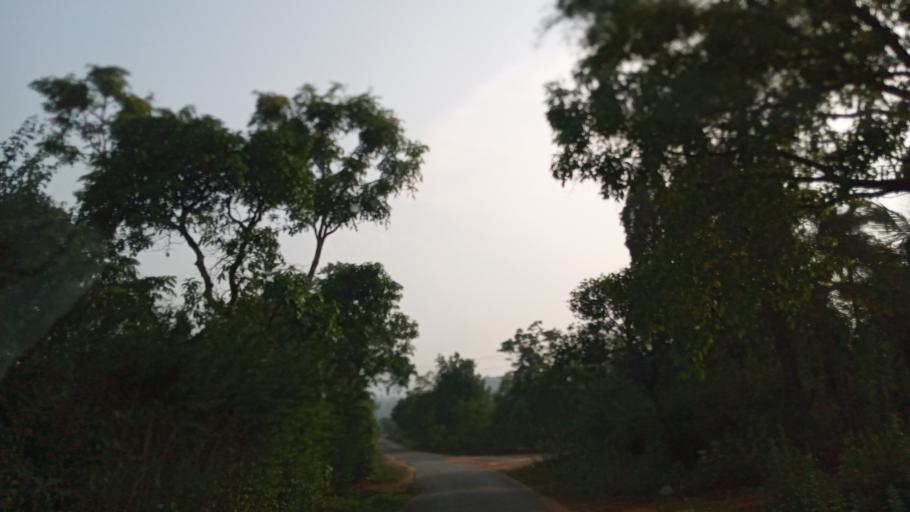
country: IN
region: Karnataka
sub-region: Chikmagalur
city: Mudigere
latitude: 13.0055
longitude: 75.6273
